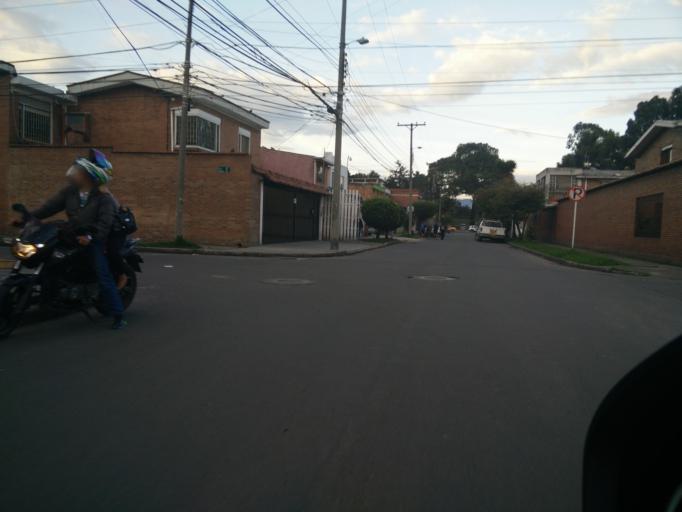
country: CO
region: Bogota D.C.
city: Bogota
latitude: 4.6456
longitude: -74.0918
